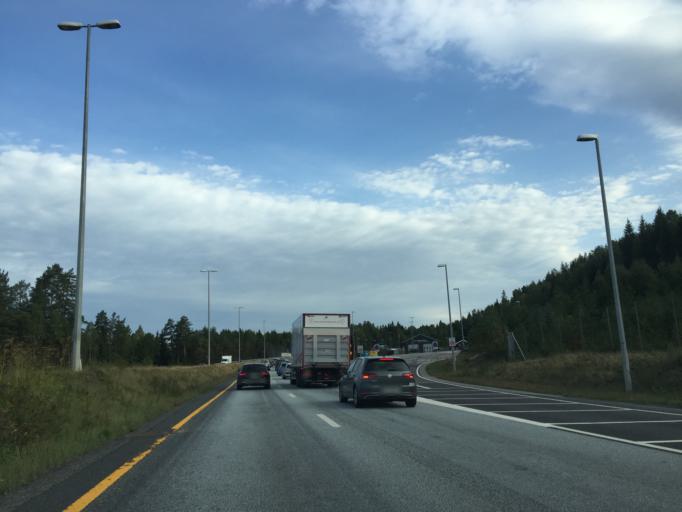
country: NO
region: Akershus
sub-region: Oppegard
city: Kolbotn
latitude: 59.8099
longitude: 10.8405
